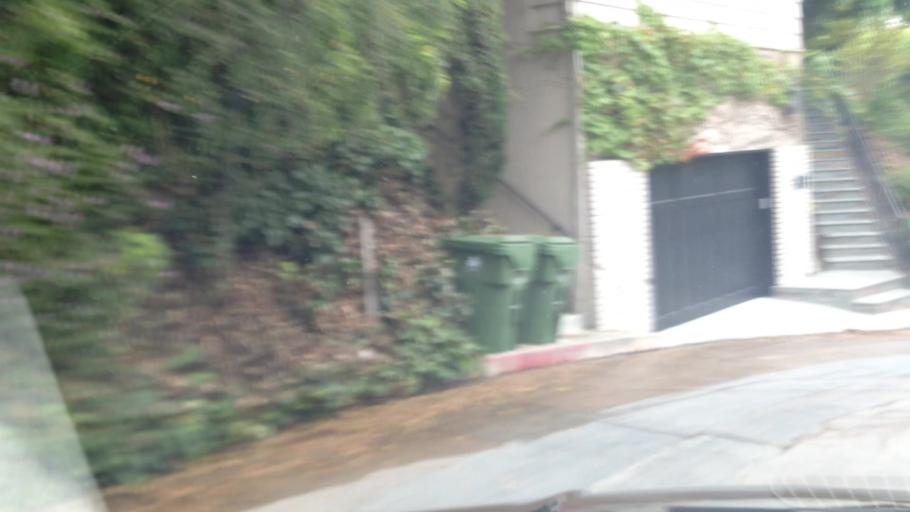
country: US
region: California
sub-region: Los Angeles County
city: Hollywood
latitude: 34.1150
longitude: -118.3435
